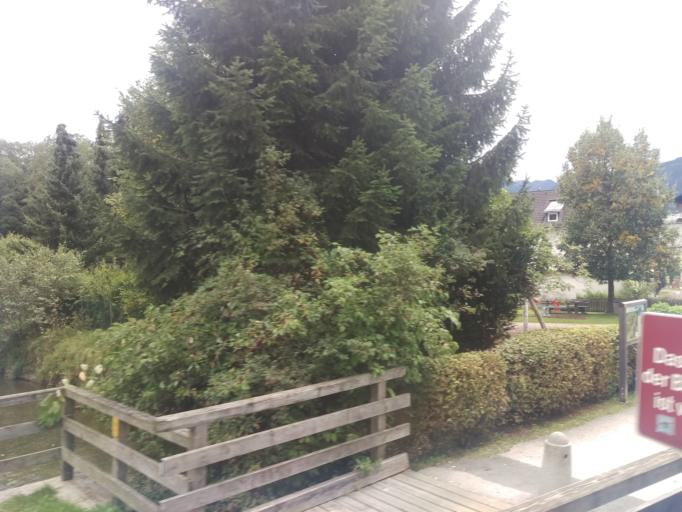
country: AT
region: Salzburg
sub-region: Politischer Bezirk Zell am See
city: Zell am See
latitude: 47.3025
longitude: 12.7947
